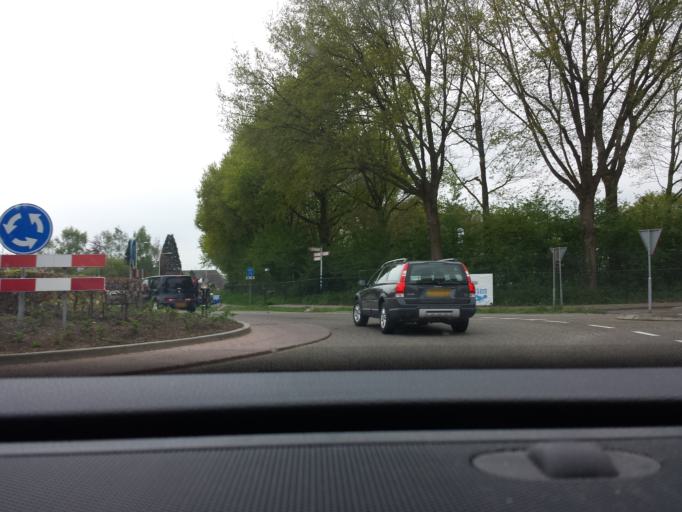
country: NL
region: Gelderland
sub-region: Gemeente Bronckhorst
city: Hengelo
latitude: 52.0449
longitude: 6.3061
